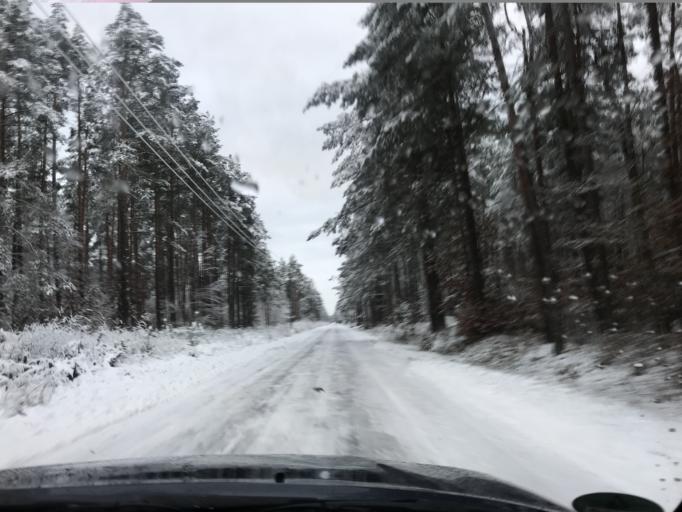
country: PL
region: Pomeranian Voivodeship
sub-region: Powiat bytowski
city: Czarna Dabrowka
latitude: 54.2874
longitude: 17.6014
